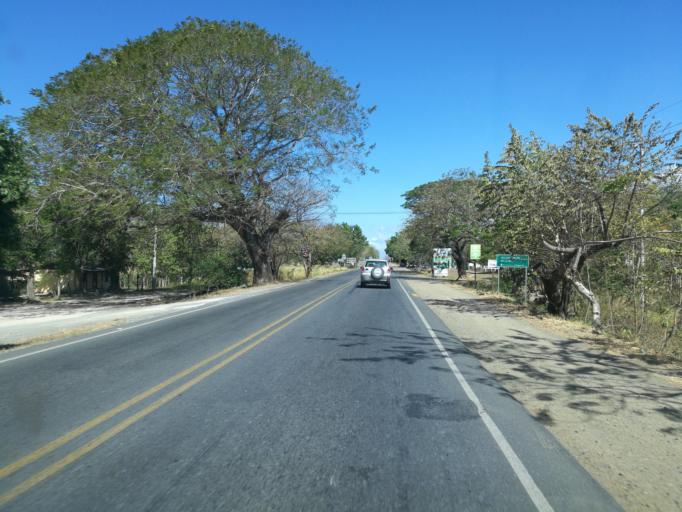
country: CR
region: Guanacaste
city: Liberia
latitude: 10.6593
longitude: -85.4694
